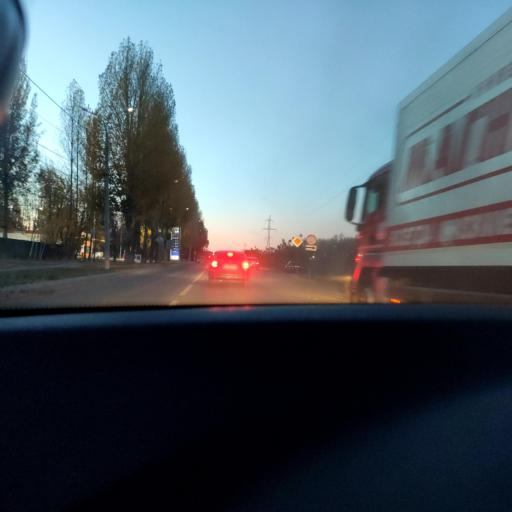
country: RU
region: Samara
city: Petra-Dubrava
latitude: 53.3051
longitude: 50.2805
